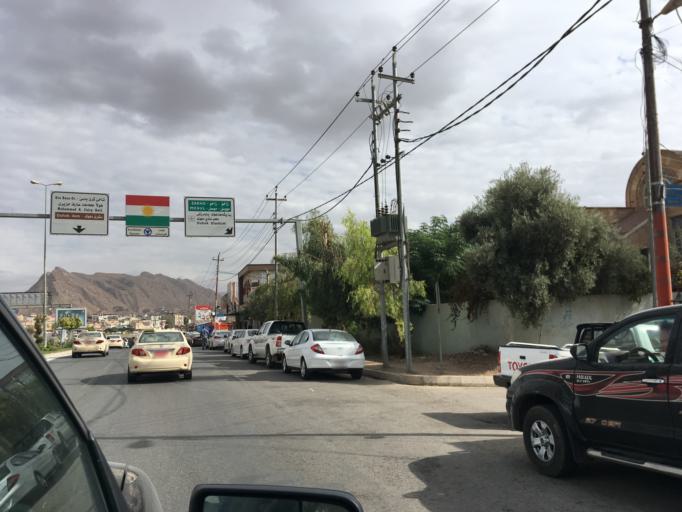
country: IQ
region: Dahuk
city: Dihok
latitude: 36.8674
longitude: 42.9746
